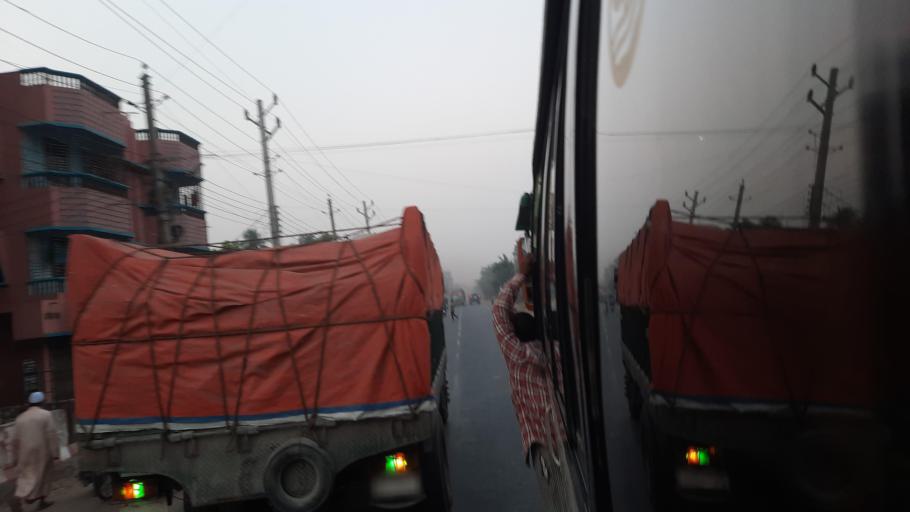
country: BD
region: Khulna
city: Jessore
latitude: 23.1720
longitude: 89.1925
